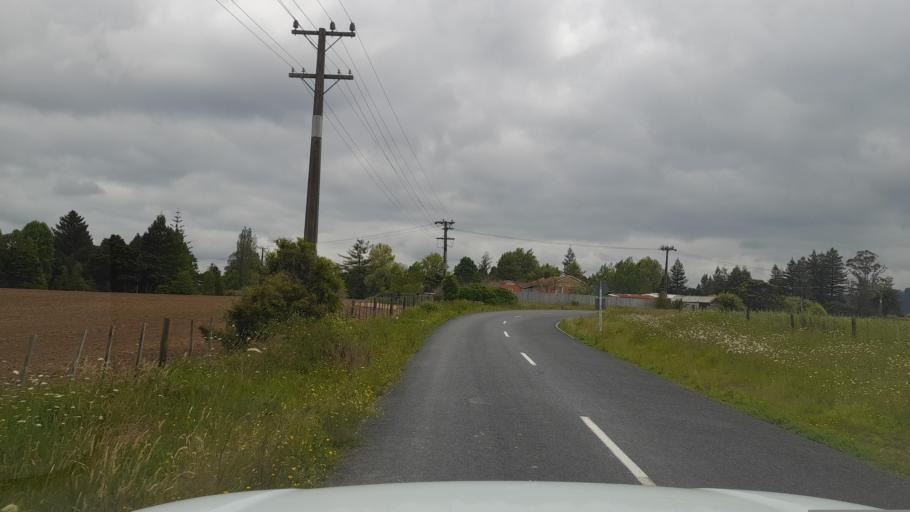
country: NZ
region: Northland
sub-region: Far North District
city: Waimate North
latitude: -35.4037
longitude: 173.8099
